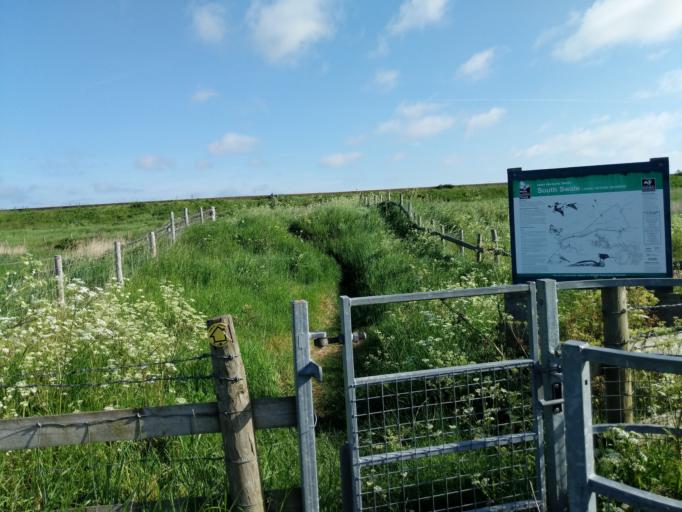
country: GB
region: England
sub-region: Kent
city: Faversham
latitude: 51.3428
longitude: 0.9188
